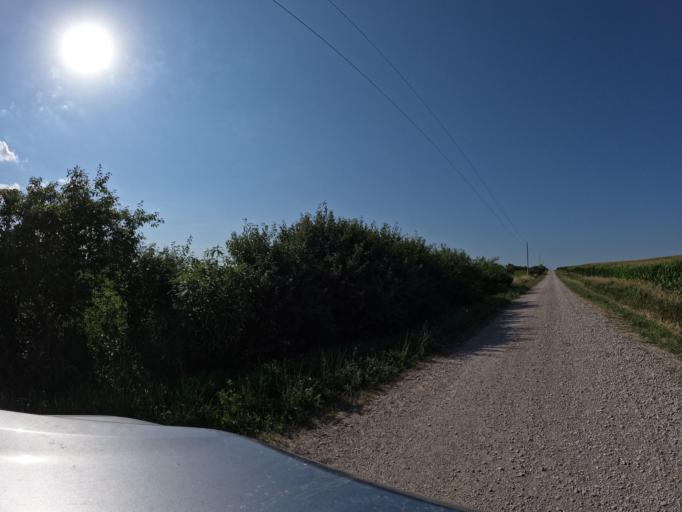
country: US
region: Iowa
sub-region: Appanoose County
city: Centerville
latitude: 40.7180
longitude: -93.0159
